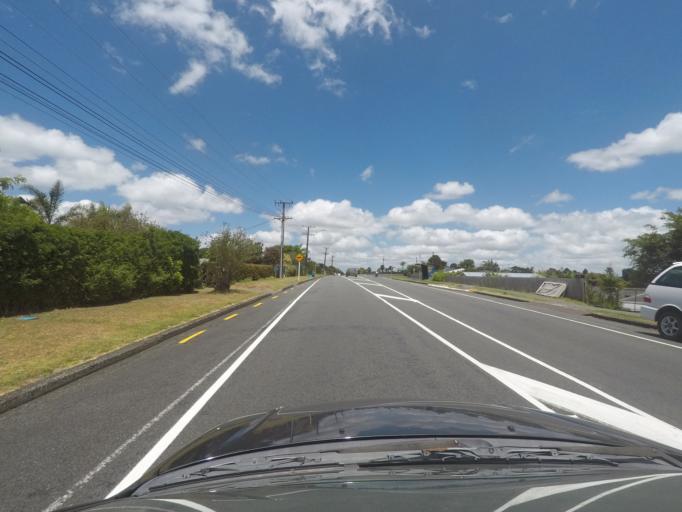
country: NZ
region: Northland
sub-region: Whangarei
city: Whangarei
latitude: -35.7634
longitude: 174.3672
